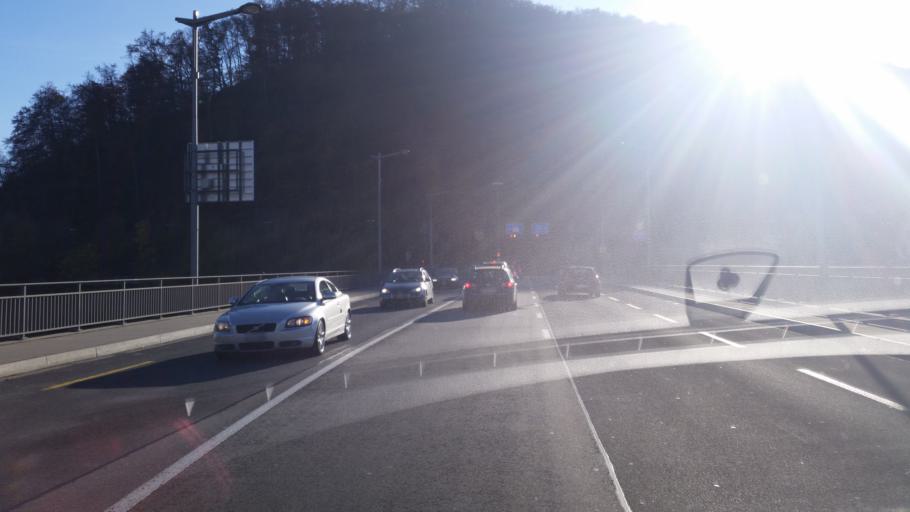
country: CH
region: Aargau
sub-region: Bezirk Baden
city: Obersiggenthal
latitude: 47.4837
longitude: 8.2989
